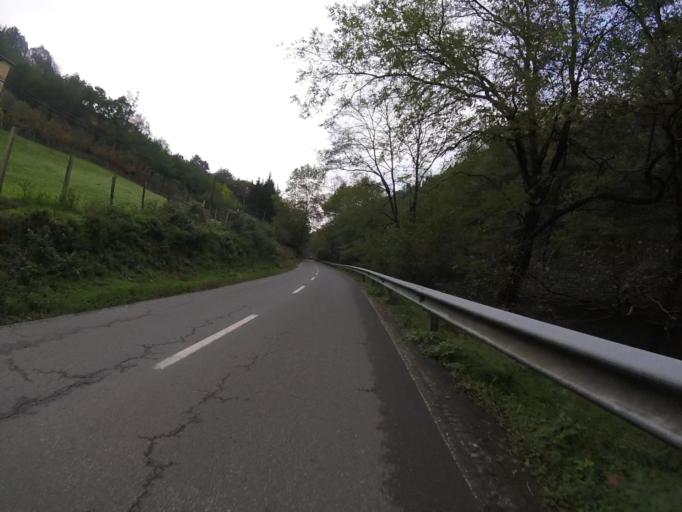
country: ES
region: Navarre
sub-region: Provincia de Navarra
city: Goizueta
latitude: 43.1852
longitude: -1.8585
